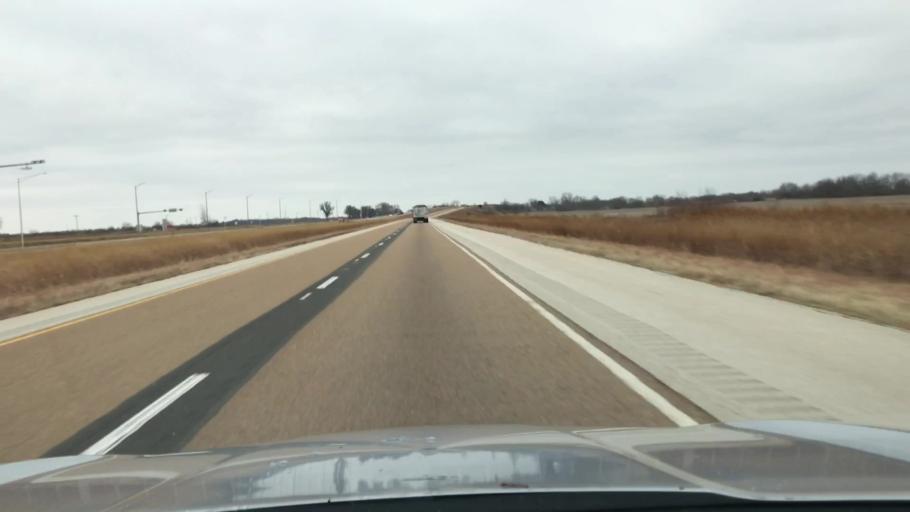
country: US
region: Illinois
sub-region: Montgomery County
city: Litchfield
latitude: 39.2264
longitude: -89.6451
